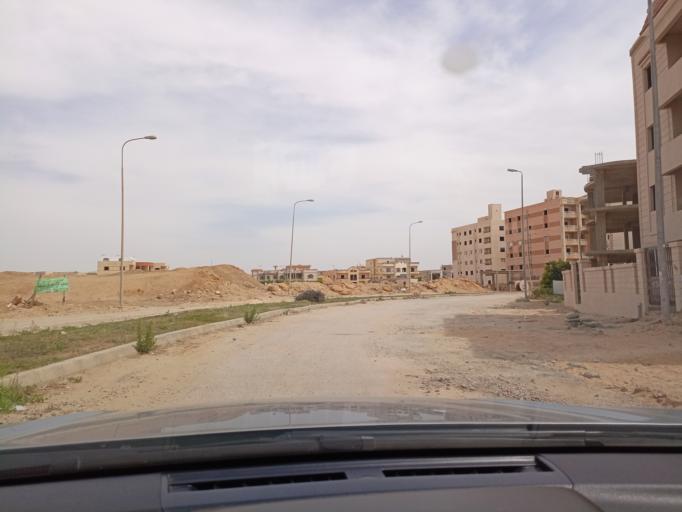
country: EG
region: Muhafazat al Qalyubiyah
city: Al Khankah
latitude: 30.2511
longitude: 31.5027
